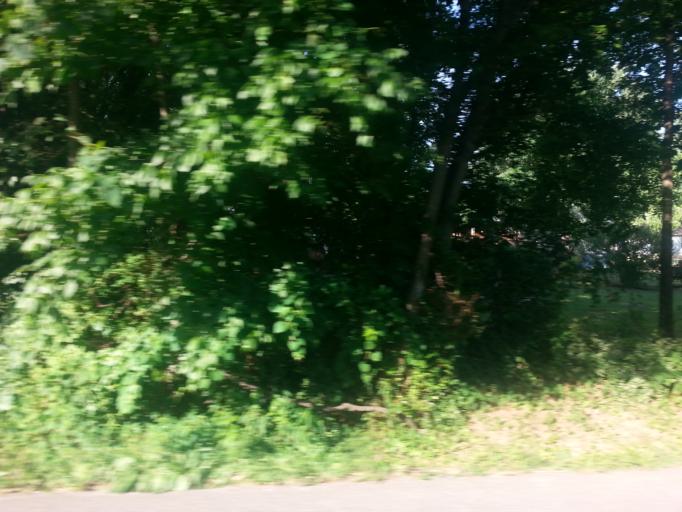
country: US
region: Tennessee
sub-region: Knox County
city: Knoxville
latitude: 35.9244
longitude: -83.9205
